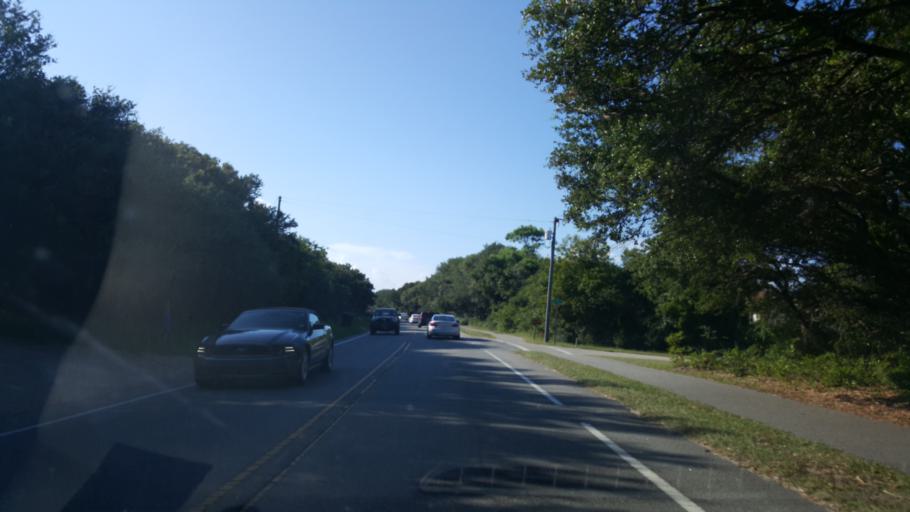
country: US
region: North Carolina
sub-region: Dare County
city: Southern Shores
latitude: 36.1402
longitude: -75.7370
